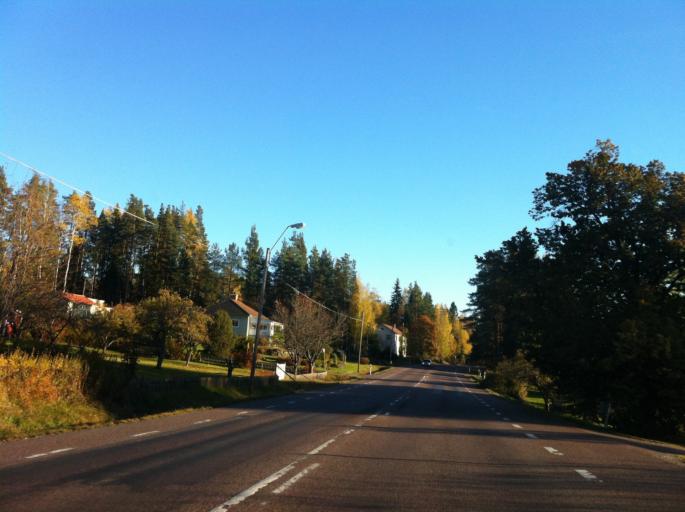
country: SE
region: Dalarna
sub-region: Faluns Kommun
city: Grycksbo
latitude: 60.6964
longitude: 15.4820
